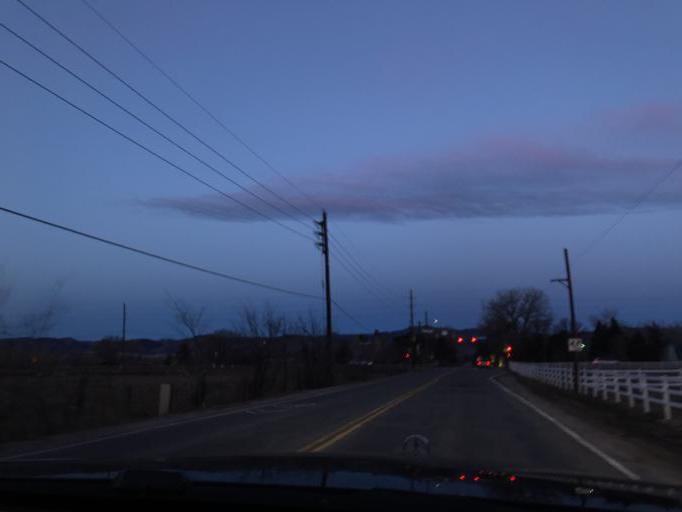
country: US
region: Colorado
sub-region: Jefferson County
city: Applewood
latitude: 39.8270
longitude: -105.1633
